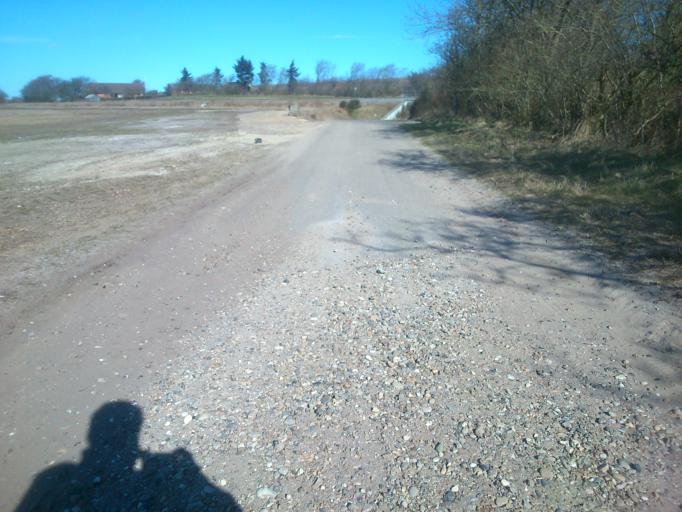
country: DK
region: Central Jutland
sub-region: Ringkobing-Skjern Kommune
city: Skjern
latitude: 55.9713
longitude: 8.4278
